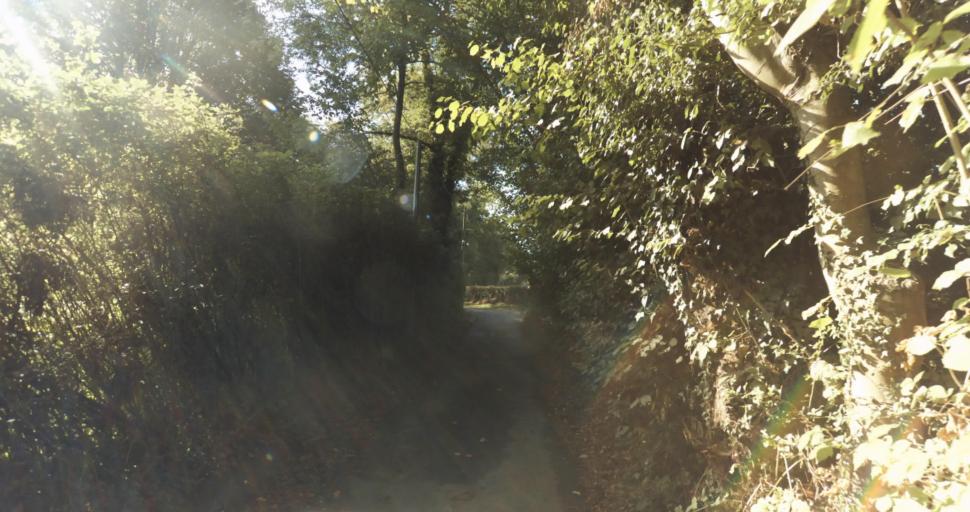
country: FR
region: Lower Normandy
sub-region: Departement de l'Orne
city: Vimoutiers
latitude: 48.9222
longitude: 0.3039
